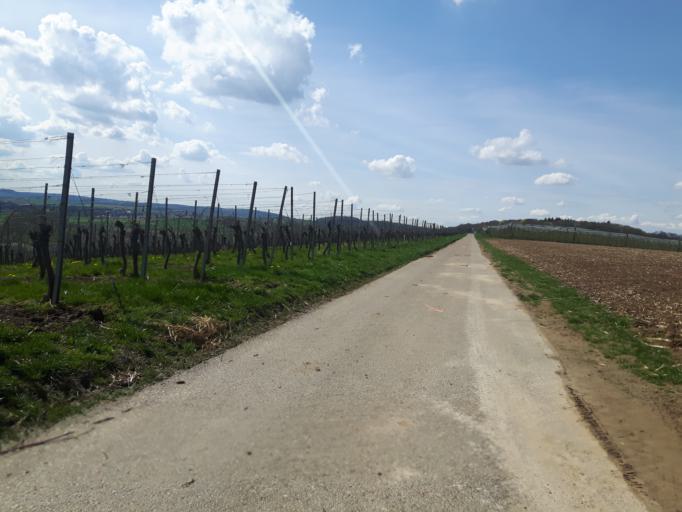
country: DE
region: Baden-Wuerttemberg
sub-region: Regierungsbezirk Stuttgart
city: Schwaigern
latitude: 49.1413
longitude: 9.0358
